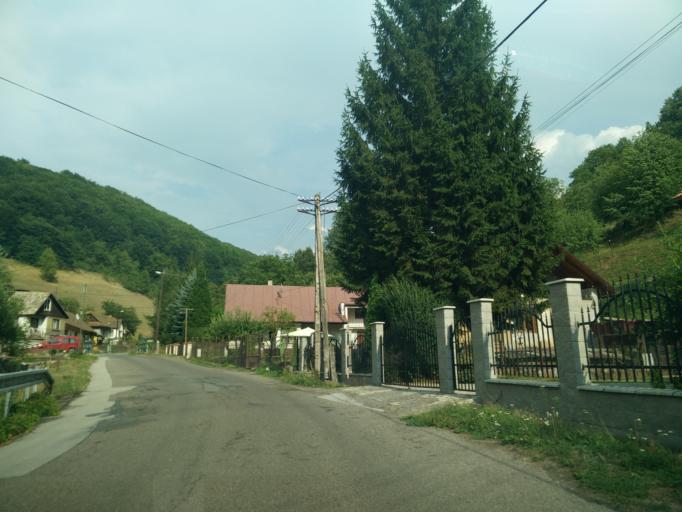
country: SK
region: Banskobystricky
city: Zarnovica
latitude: 48.5000
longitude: 18.8098
